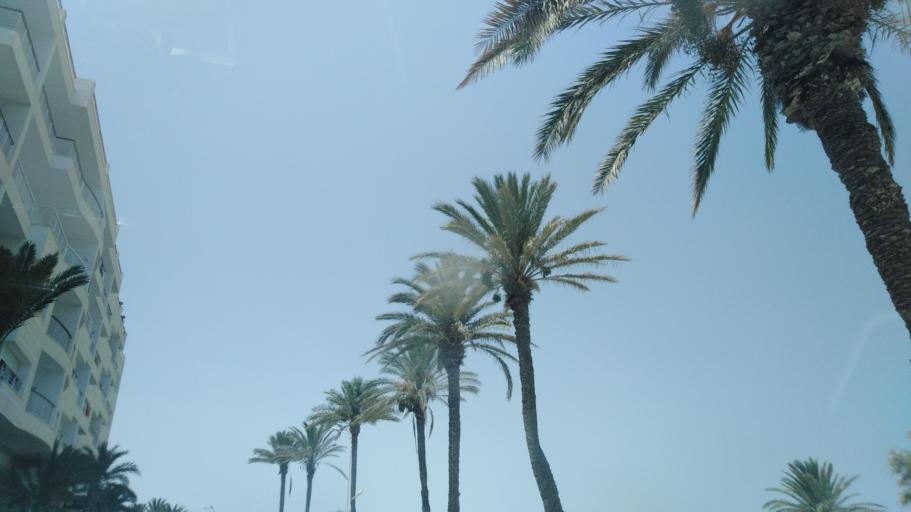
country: TN
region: Al Mahdiyah
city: Mahdia
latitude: 35.5234
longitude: 11.0407
